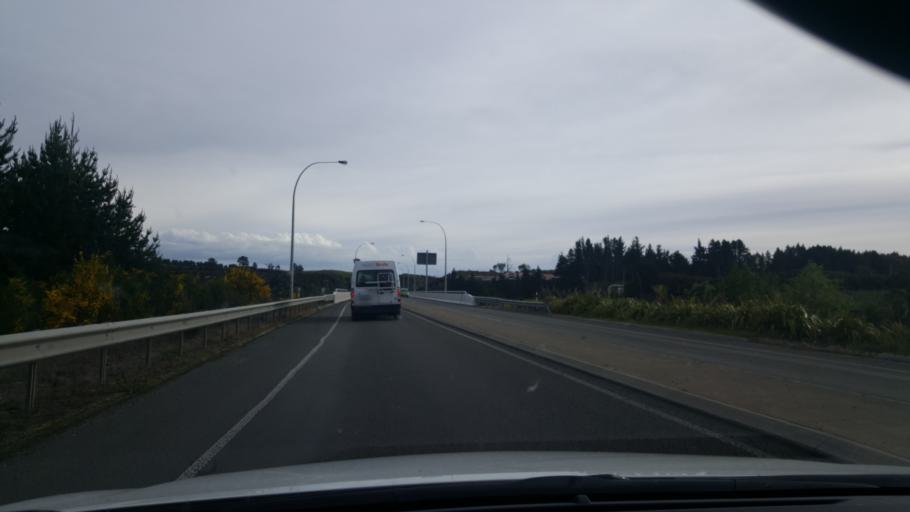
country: NZ
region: Waikato
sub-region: Taupo District
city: Taupo
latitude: -38.6241
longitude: 176.0996
